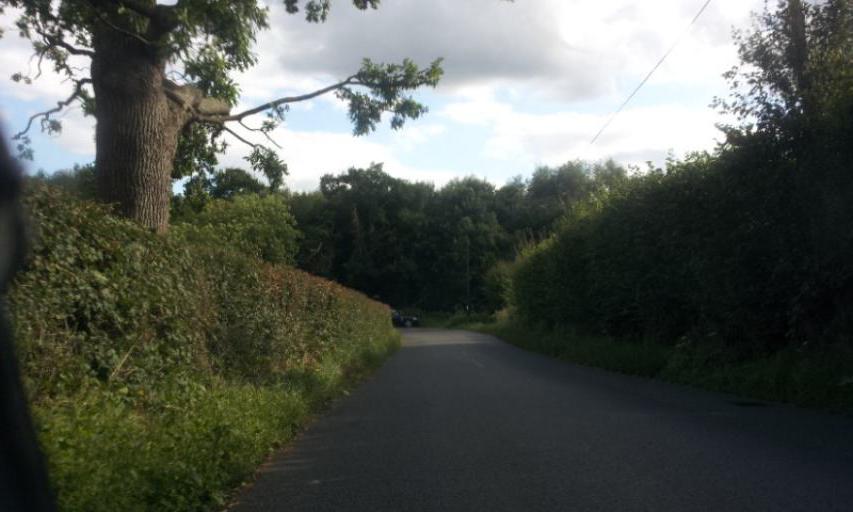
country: GB
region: England
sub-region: Kent
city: Headcorn
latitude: 51.1711
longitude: 0.6057
